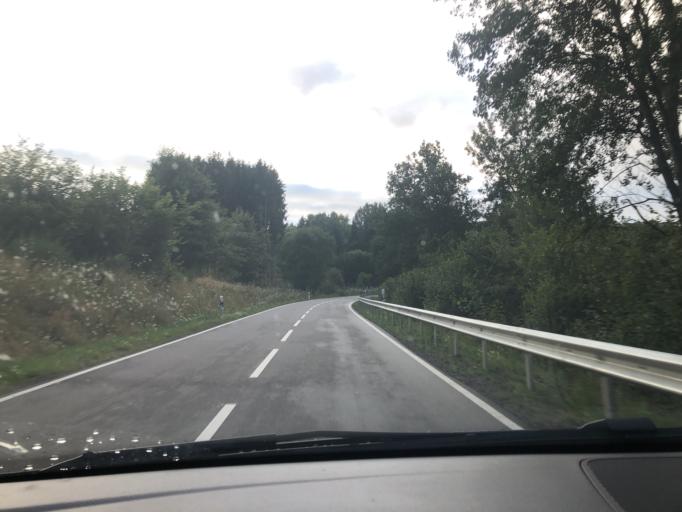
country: DE
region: Rheinland-Pfalz
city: Grimburg
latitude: 49.6152
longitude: 6.8844
